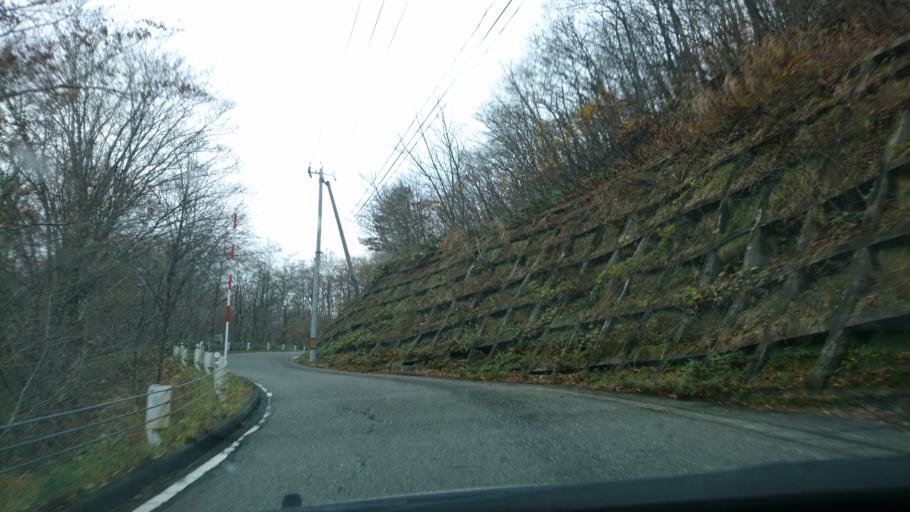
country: JP
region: Iwate
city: Ichinoseki
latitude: 38.9167
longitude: 140.8458
